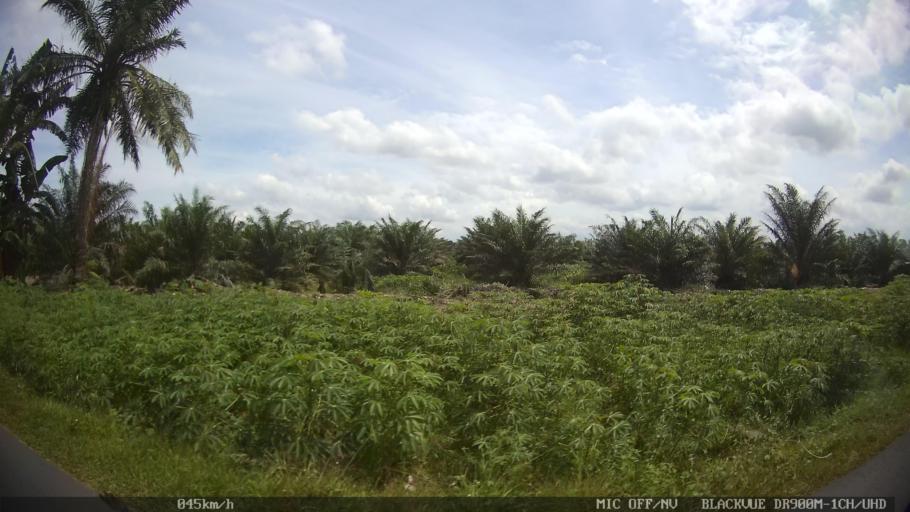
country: ID
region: North Sumatra
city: Percut
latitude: 3.5892
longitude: 98.8681
